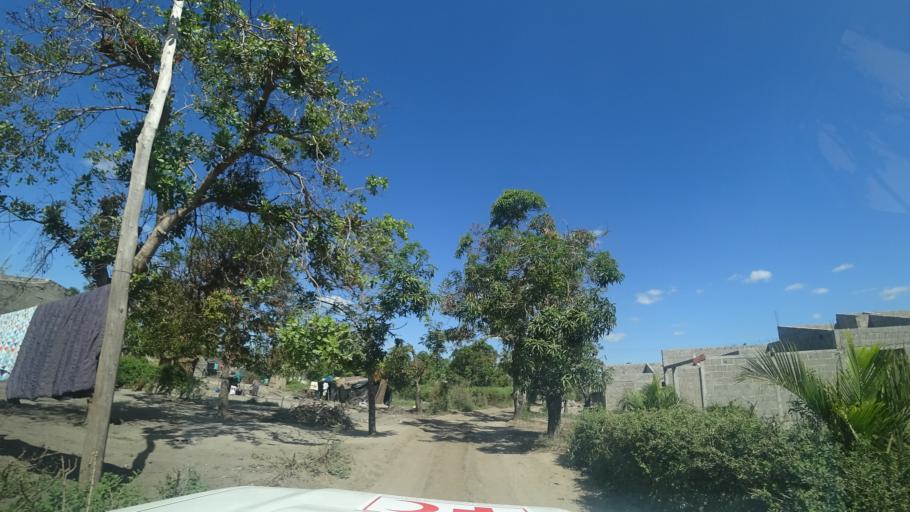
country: MZ
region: Sofala
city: Dondo
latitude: -19.4922
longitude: 34.5993
